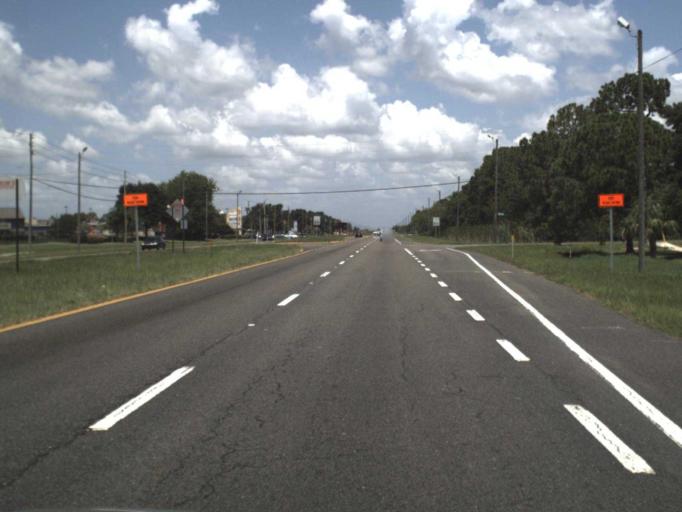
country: US
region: Florida
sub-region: Pinellas County
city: Gandy
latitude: 27.8694
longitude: -82.6387
